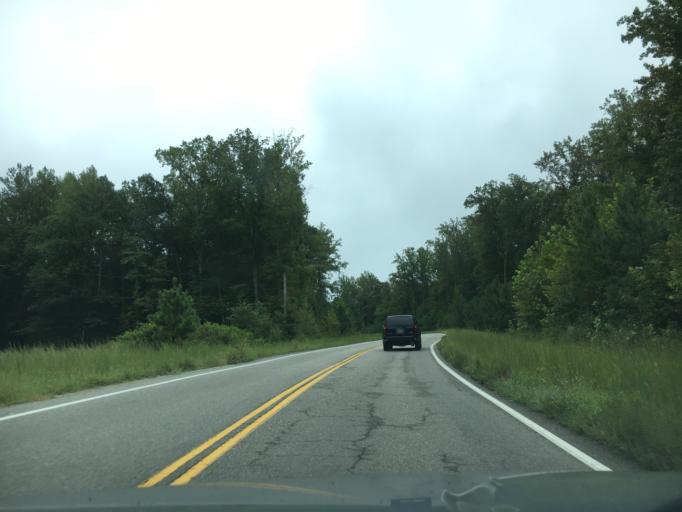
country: US
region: Virginia
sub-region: Chesterfield County
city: Woodlake
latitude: 37.5000
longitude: -77.7804
